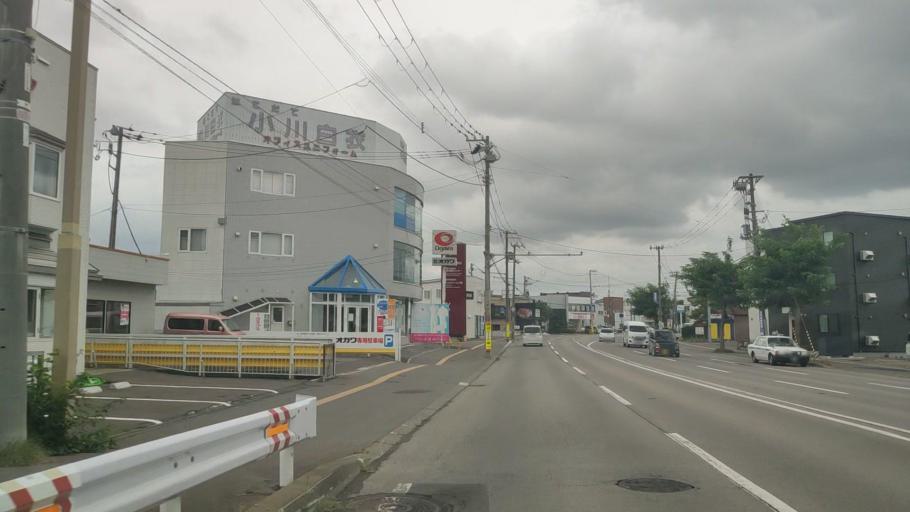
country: JP
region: Hokkaido
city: Hakodate
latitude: 41.7984
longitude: 140.7506
